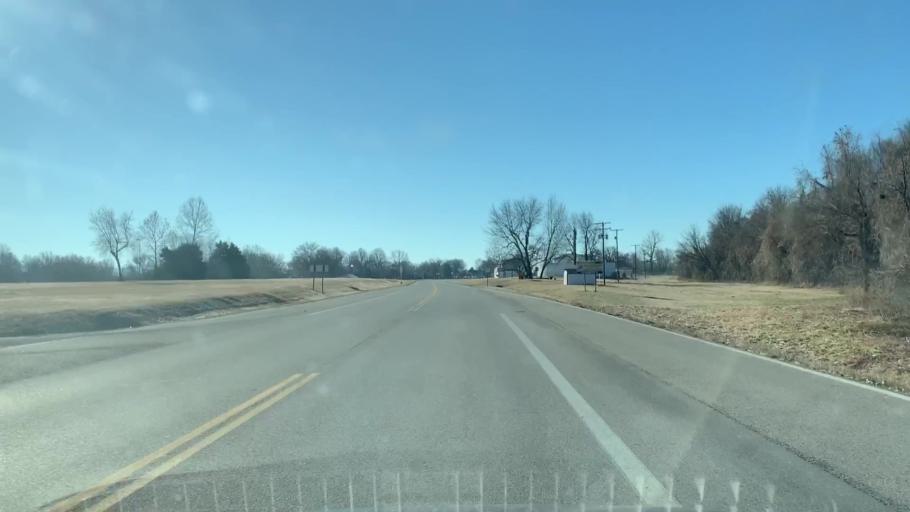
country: US
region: Kansas
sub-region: Cherokee County
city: Baxter Springs
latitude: 37.0378
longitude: -94.7352
